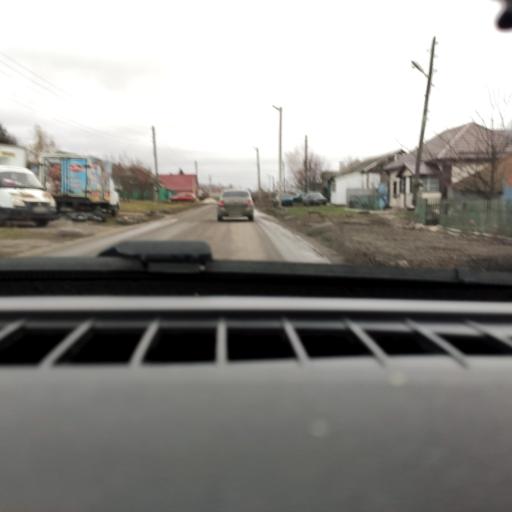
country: RU
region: Voronezj
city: Devitsa
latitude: 51.6387
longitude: 38.9363
